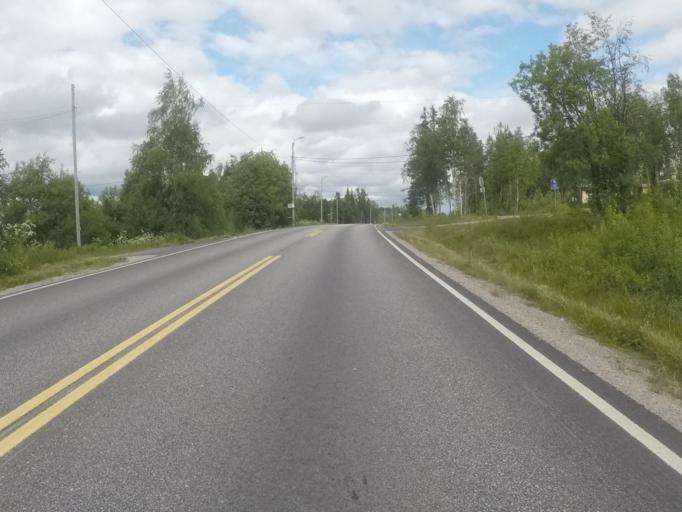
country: FI
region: Lapland
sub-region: Tunturi-Lappi
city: Enontekioe
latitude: 68.2822
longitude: 23.0817
